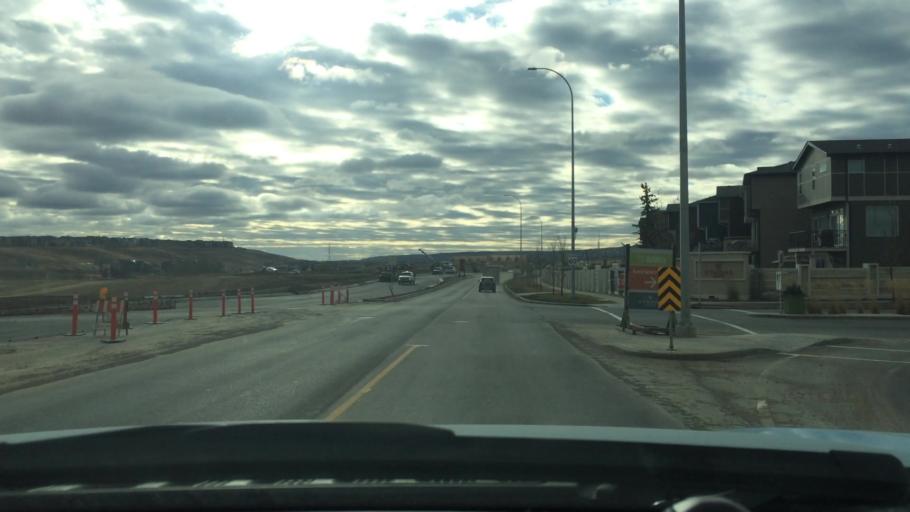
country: CA
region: Alberta
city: Calgary
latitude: 51.1810
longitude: -114.1342
